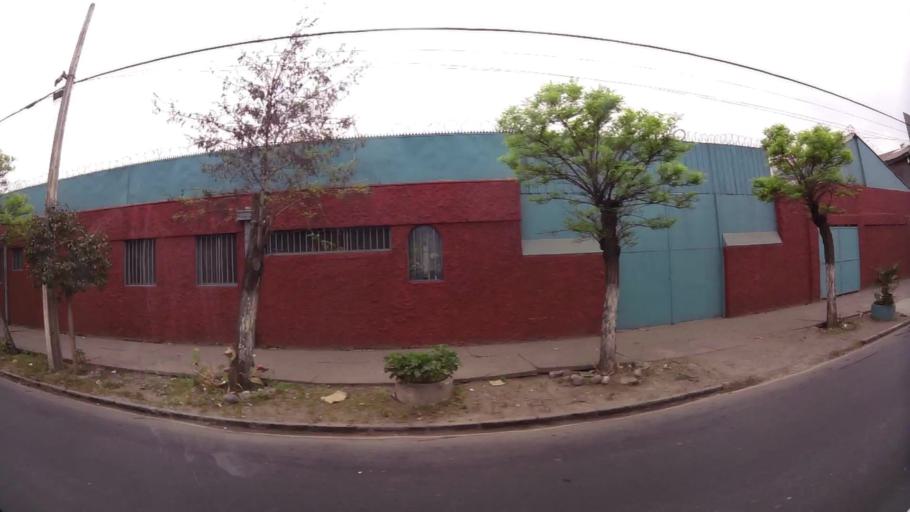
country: CL
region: Santiago Metropolitan
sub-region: Provincia de Santiago
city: Santiago
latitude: -33.4786
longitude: -70.6682
